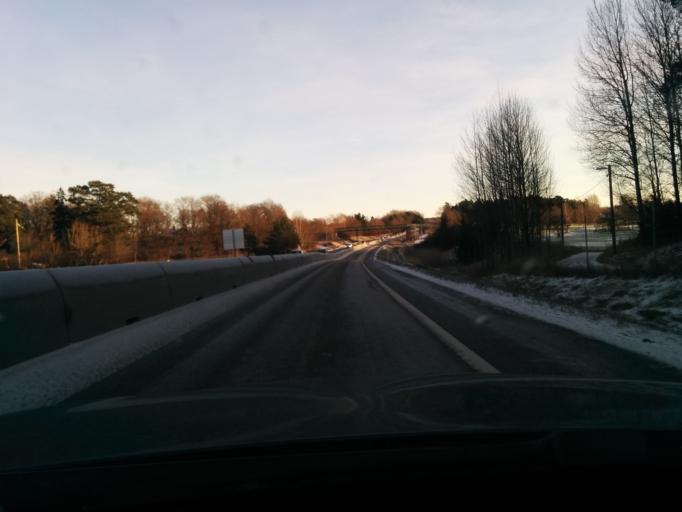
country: SE
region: Stockholm
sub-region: Upplands Vasby Kommun
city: Upplands Vaesby
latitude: 59.4748
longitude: 17.8877
